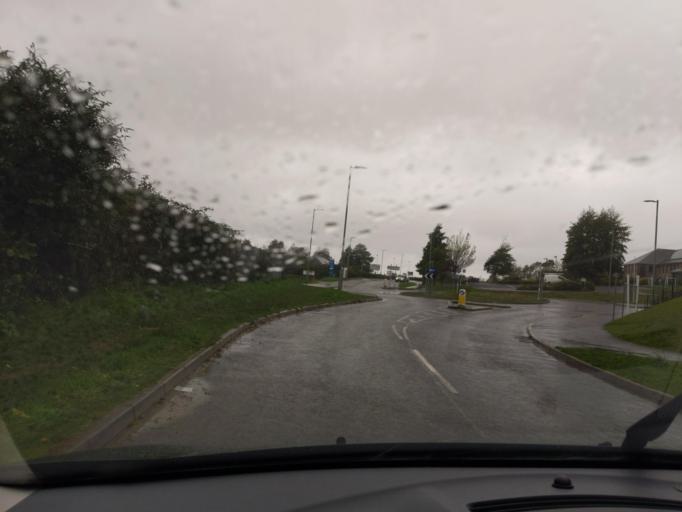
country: GB
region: England
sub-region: Cornwall
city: Wadebridge
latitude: 50.5210
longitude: -4.8227
